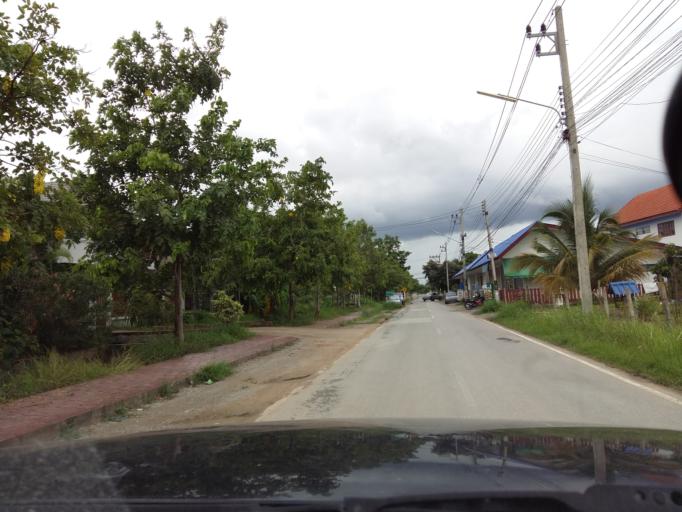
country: TH
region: Chiang Mai
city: Chiang Mai
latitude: 18.7518
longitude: 98.9771
